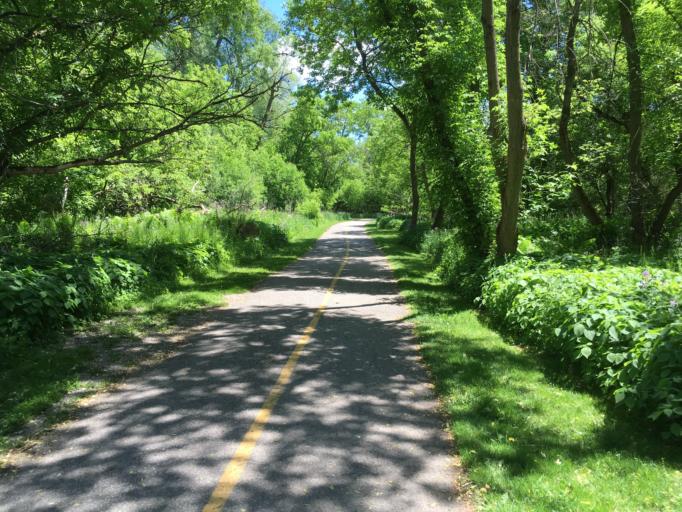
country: CA
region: Ontario
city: Oshawa
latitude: 43.8668
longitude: -78.8437
